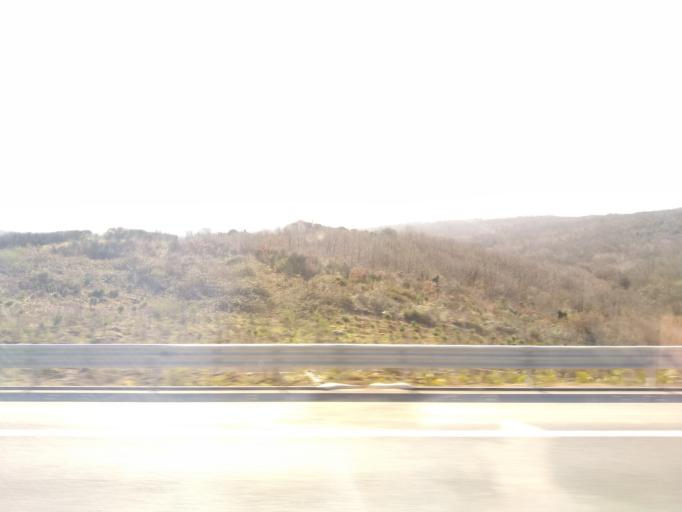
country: TR
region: Istanbul
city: Mahmut Sevket Pasa
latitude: 41.1826
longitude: 29.2301
